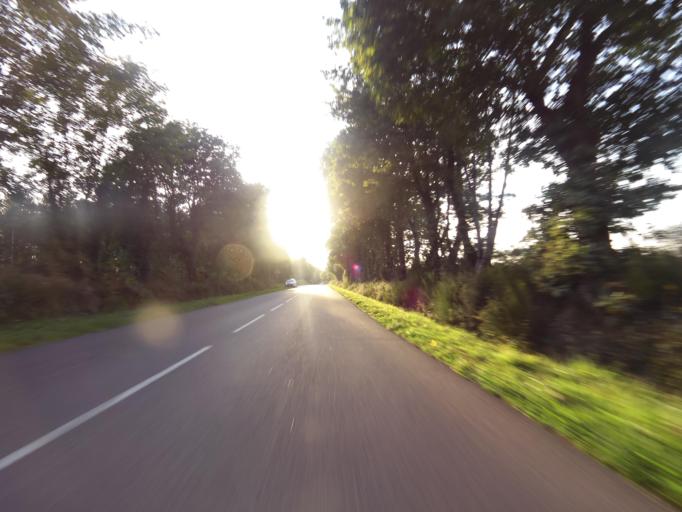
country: FR
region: Brittany
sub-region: Departement du Morbihan
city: Theix
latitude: 47.6359
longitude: -2.6168
